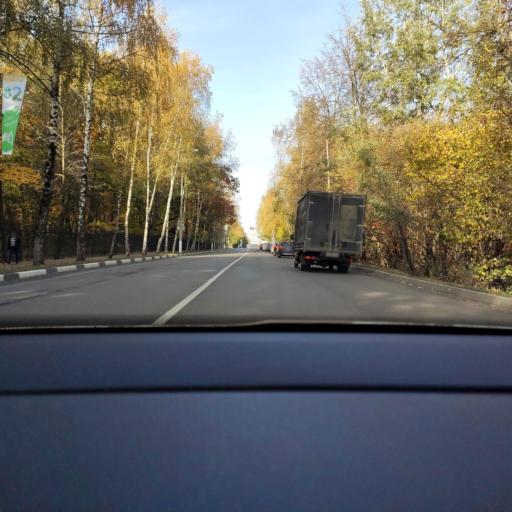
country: RU
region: Moskovskaya
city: Ivanteyevka
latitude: 55.9790
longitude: 37.8985
